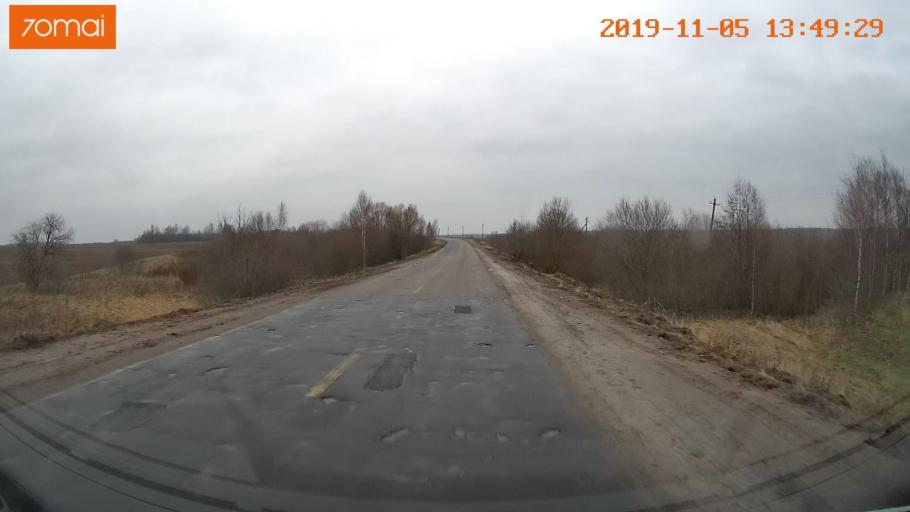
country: RU
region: Ivanovo
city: Kaminskiy
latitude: 57.0110
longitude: 41.4098
